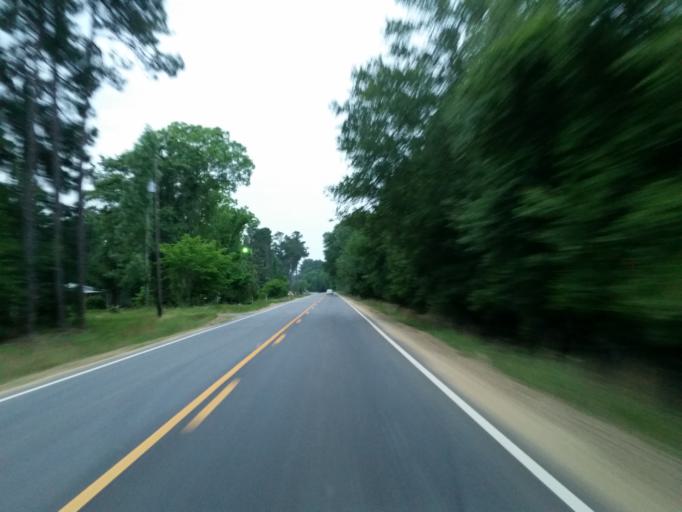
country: US
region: Georgia
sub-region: Turner County
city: Ashburn
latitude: 31.7647
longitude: -83.6855
